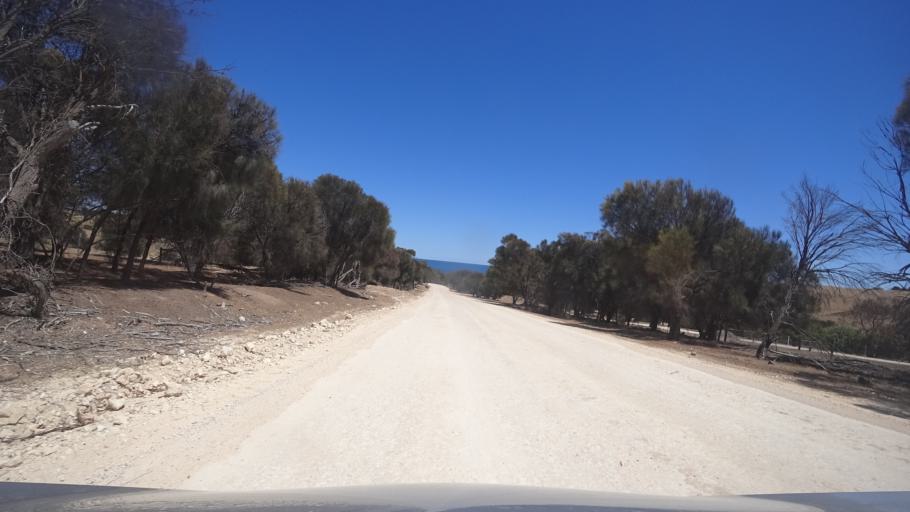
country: AU
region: South Australia
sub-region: Kangaroo Island
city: Kingscote
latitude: -35.6257
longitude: 137.2103
